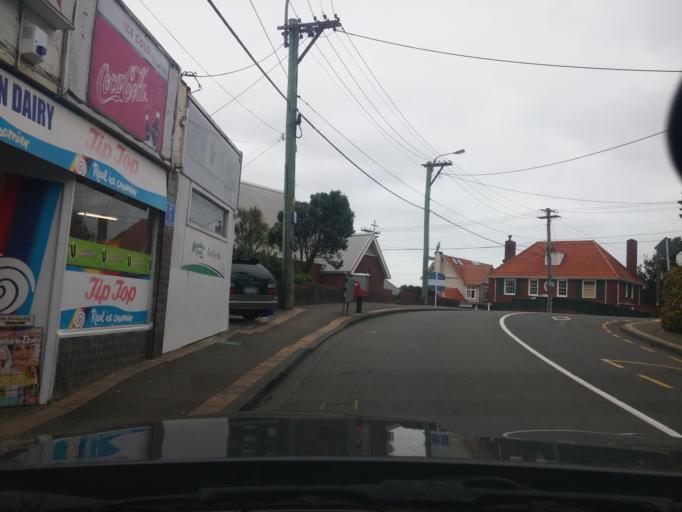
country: NZ
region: Wellington
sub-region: Wellington City
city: Kelburn
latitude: -41.2617
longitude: 174.7751
